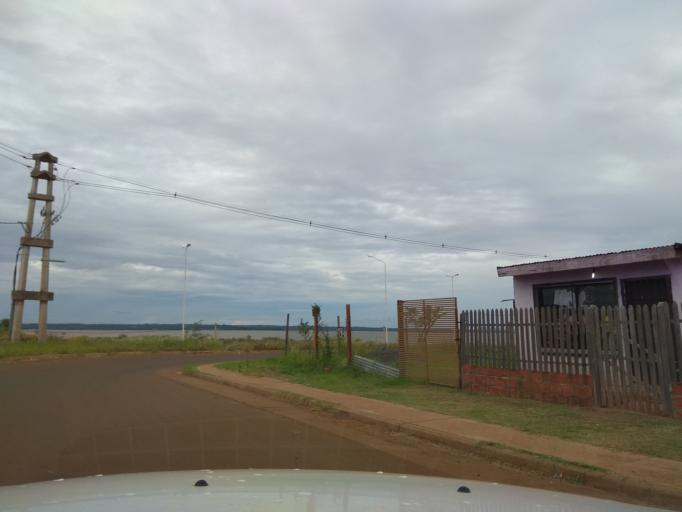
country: AR
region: Misiones
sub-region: Departamento de Capital
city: Posadas
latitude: -27.4279
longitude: -55.8718
